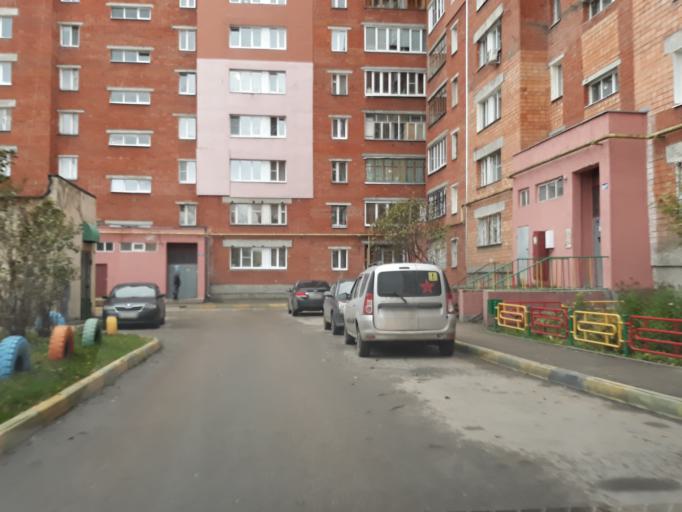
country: RU
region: Nizjnij Novgorod
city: Nizhniy Novgorod
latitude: 56.2520
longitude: 43.9871
